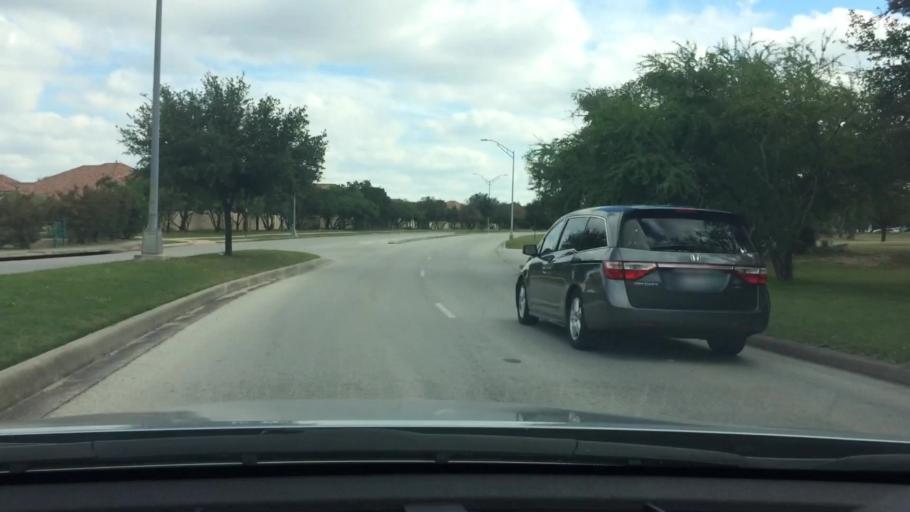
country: US
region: Texas
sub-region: Bexar County
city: Shavano Park
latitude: 29.5901
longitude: -98.5740
